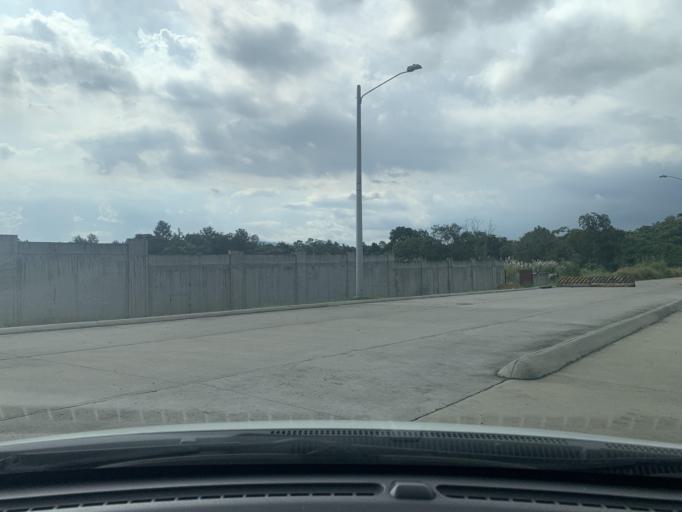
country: PA
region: Panama
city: San Miguelito
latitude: 9.0928
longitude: -79.4717
